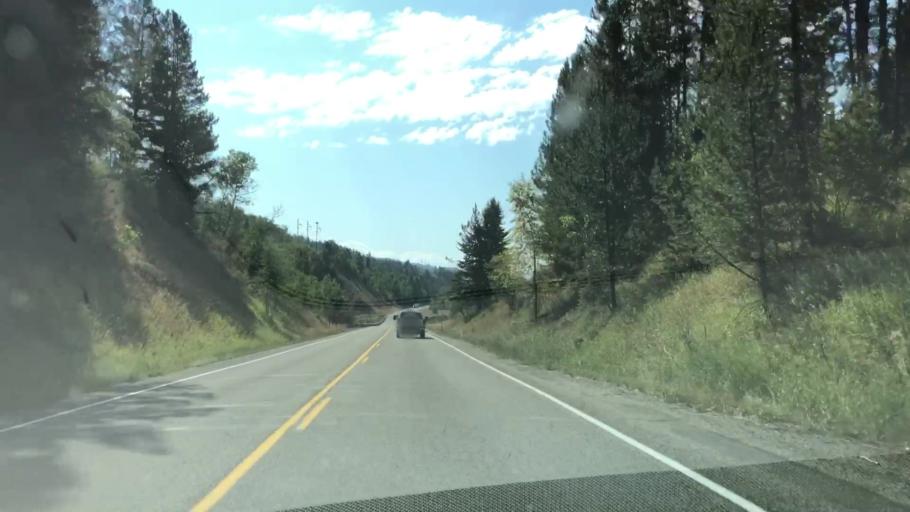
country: US
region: Idaho
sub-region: Teton County
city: Victor
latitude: 43.2960
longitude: -111.1276
